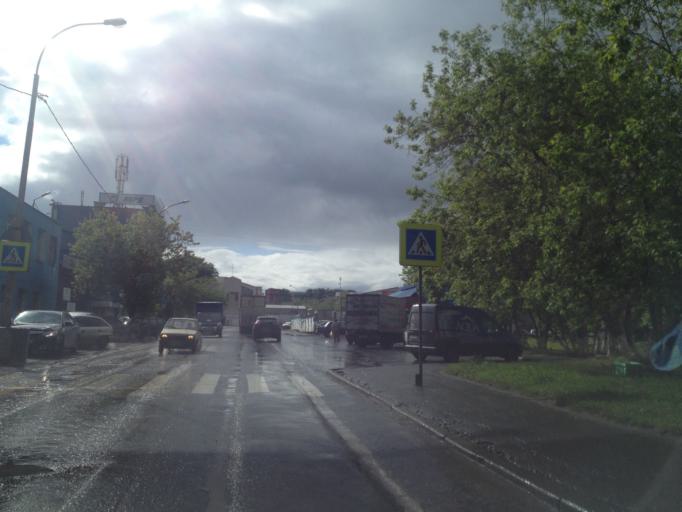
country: RU
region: Sverdlovsk
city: Yekaterinburg
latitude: 56.8634
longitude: 60.6025
